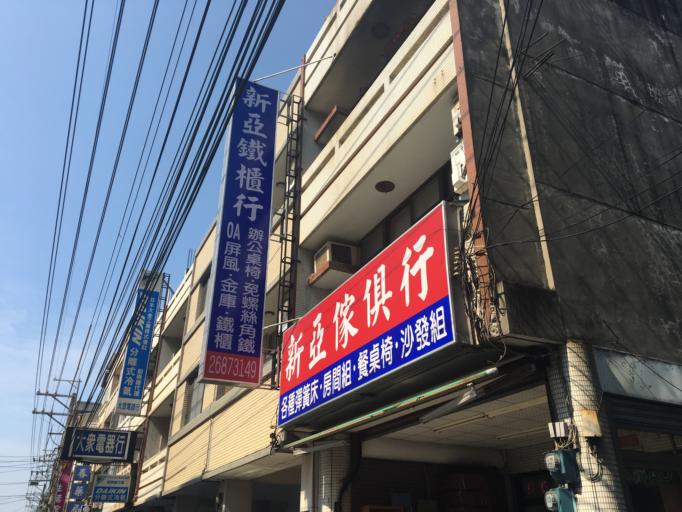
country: TW
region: Taiwan
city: Fengyuan
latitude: 24.3478
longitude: 120.6214
